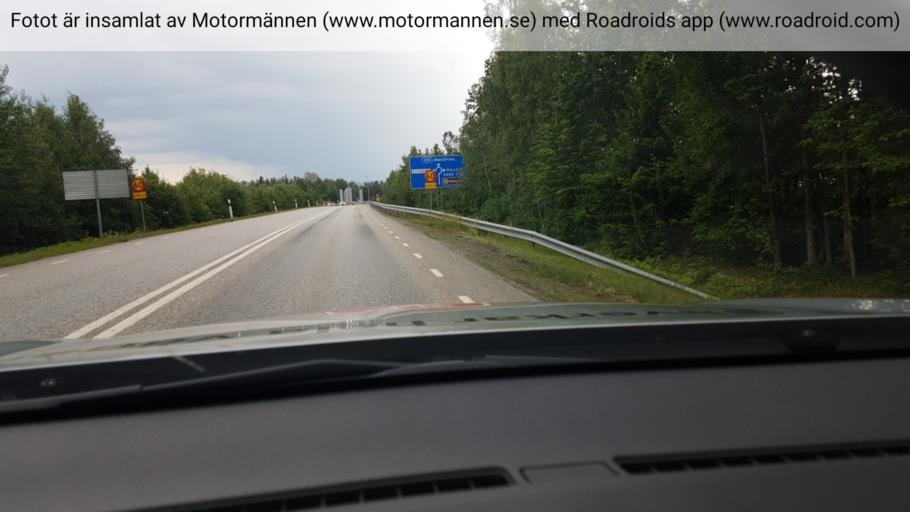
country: SE
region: Joenkoeping
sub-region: Habo Kommun
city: Habo
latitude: 57.9023
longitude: 14.1051
